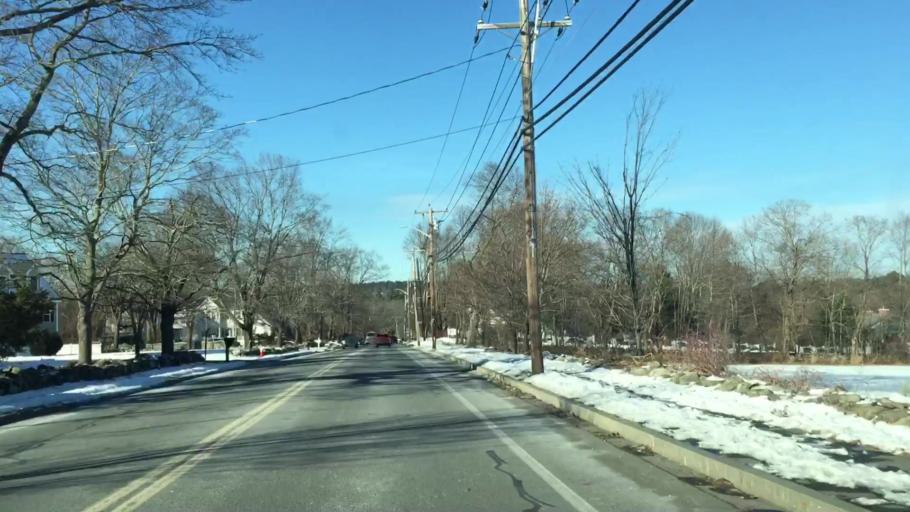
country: US
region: Massachusetts
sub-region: Middlesex County
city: Dracut
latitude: 42.6694
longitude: -71.3502
